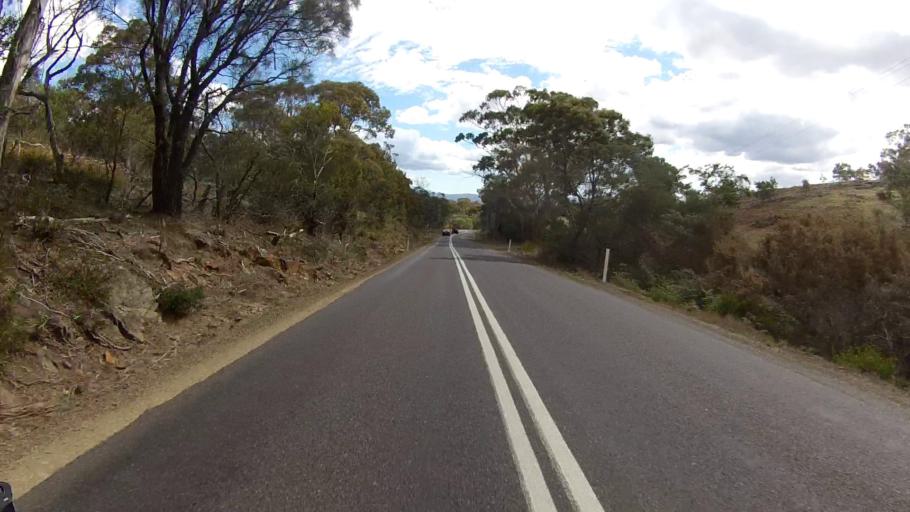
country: AU
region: Tasmania
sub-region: Break O'Day
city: St Helens
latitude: -41.9907
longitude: 148.1196
